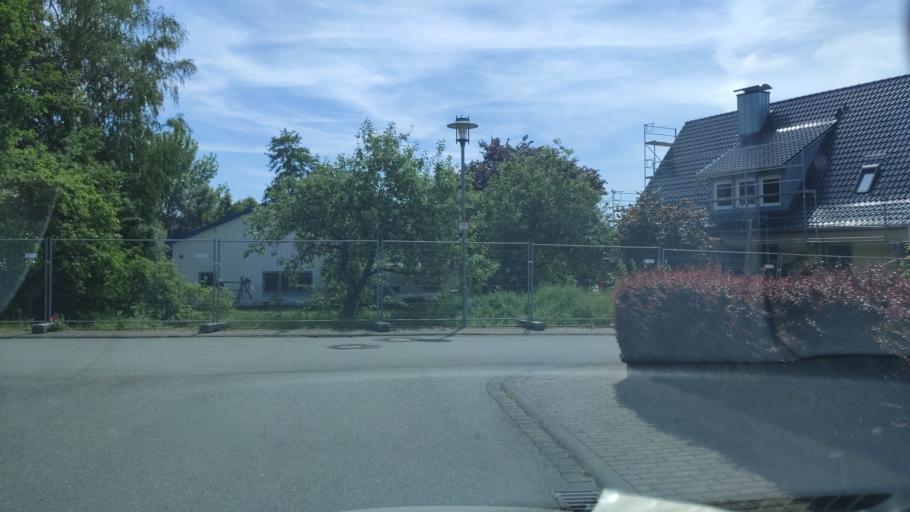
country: DE
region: North Rhine-Westphalia
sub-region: Regierungsbezirk Detmold
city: Steinheim
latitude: 51.8645
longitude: 9.0903
